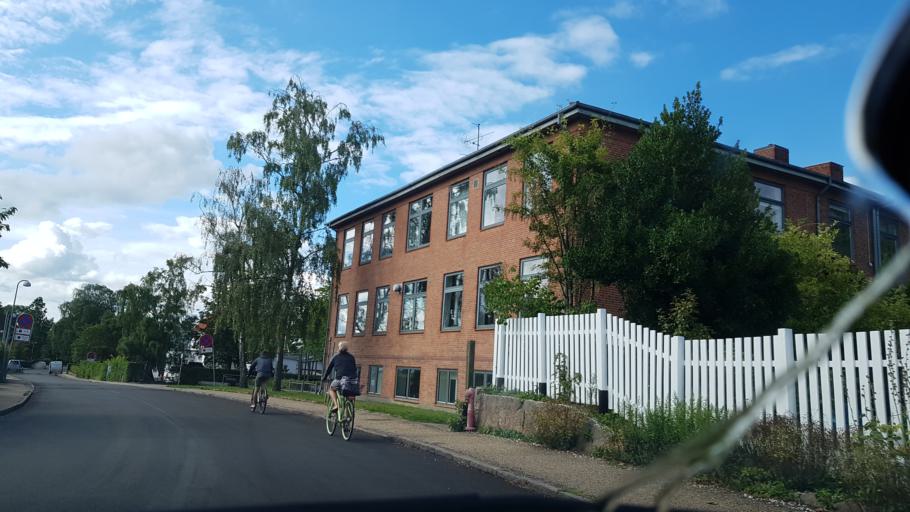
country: DK
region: Capital Region
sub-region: Helsingor Kommune
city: Espergaerde
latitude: 55.9891
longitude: 12.5537
